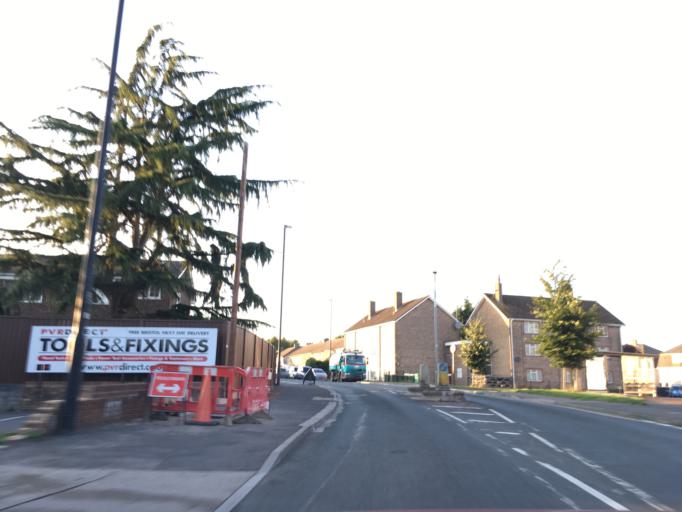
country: GB
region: England
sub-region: South Gloucestershire
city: Kingswood
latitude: 51.4363
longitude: -2.5321
